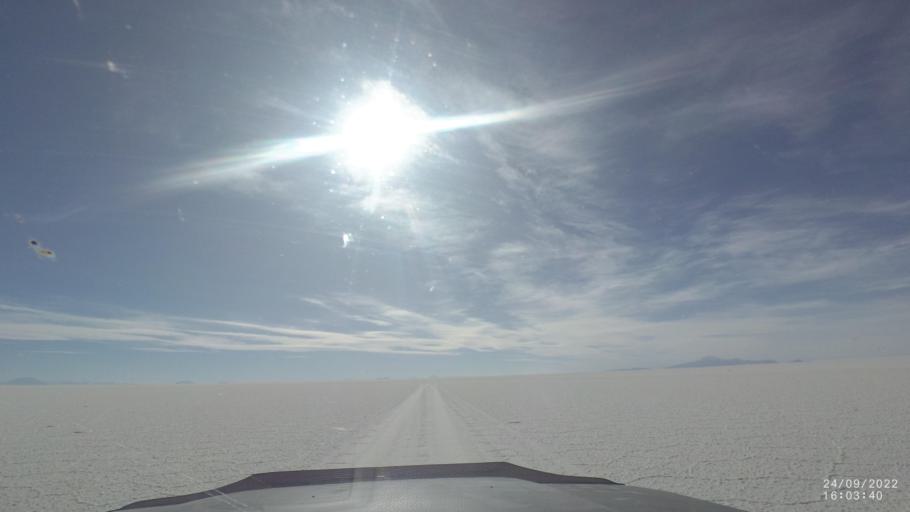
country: BO
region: Potosi
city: Colchani
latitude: -20.3127
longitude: -67.2846
